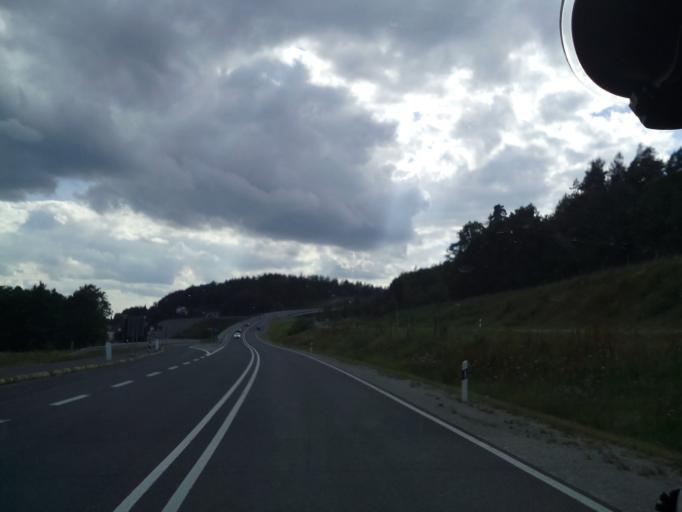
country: DE
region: Bavaria
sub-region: Upper Franconia
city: Rodental
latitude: 50.3081
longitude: 11.0680
